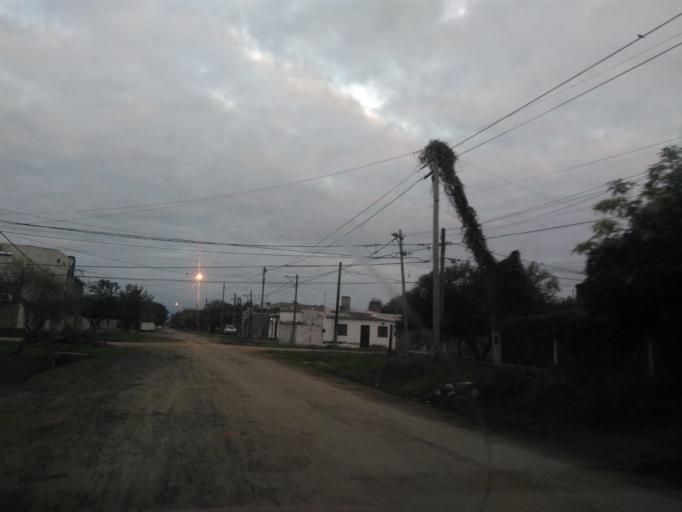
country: AR
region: Chaco
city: Resistencia
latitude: -27.4724
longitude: -58.9925
